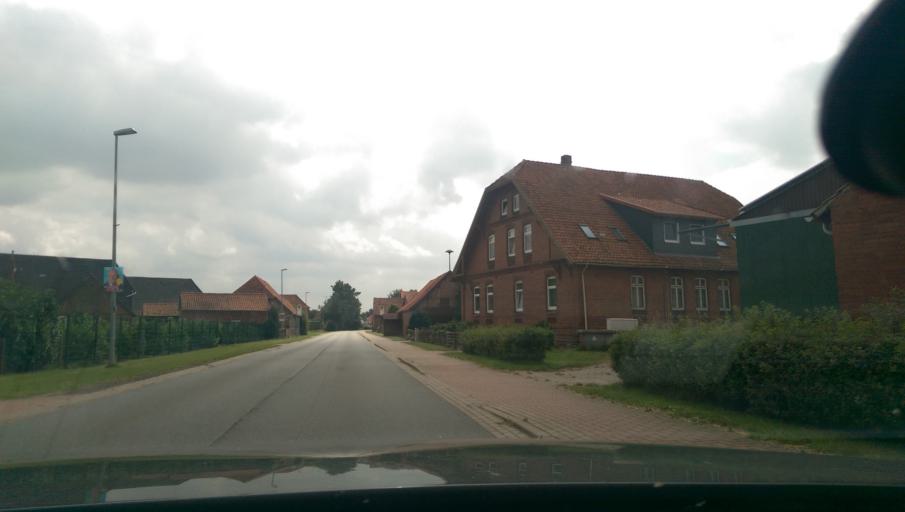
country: DE
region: Lower Saxony
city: Frankenfeld
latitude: 52.6891
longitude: 9.4826
